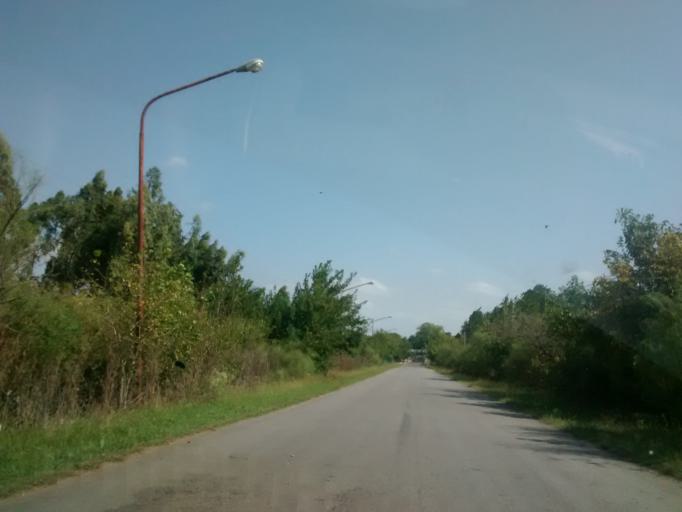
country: AR
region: Buenos Aires
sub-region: Partido de La Plata
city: La Plata
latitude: -35.0056
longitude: -57.9096
